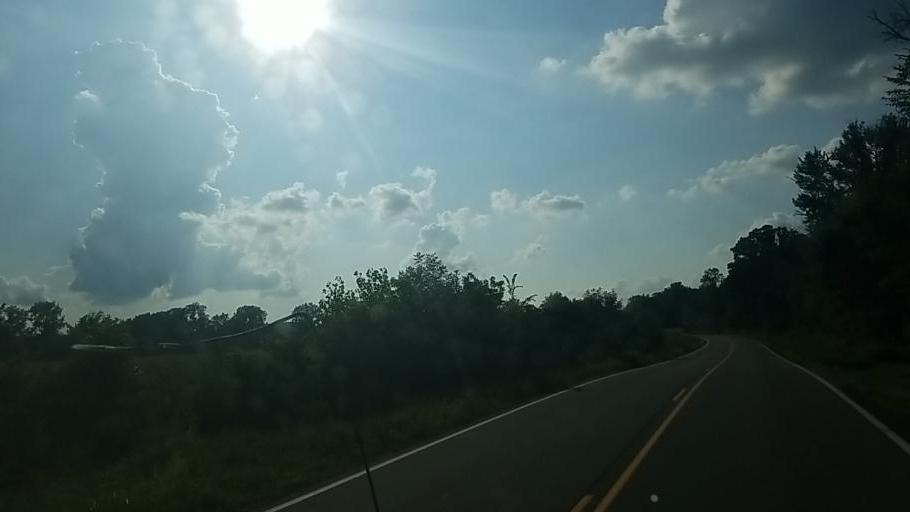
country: US
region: Ohio
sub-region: Wayne County
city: West Salem
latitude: 40.8937
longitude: -82.1451
